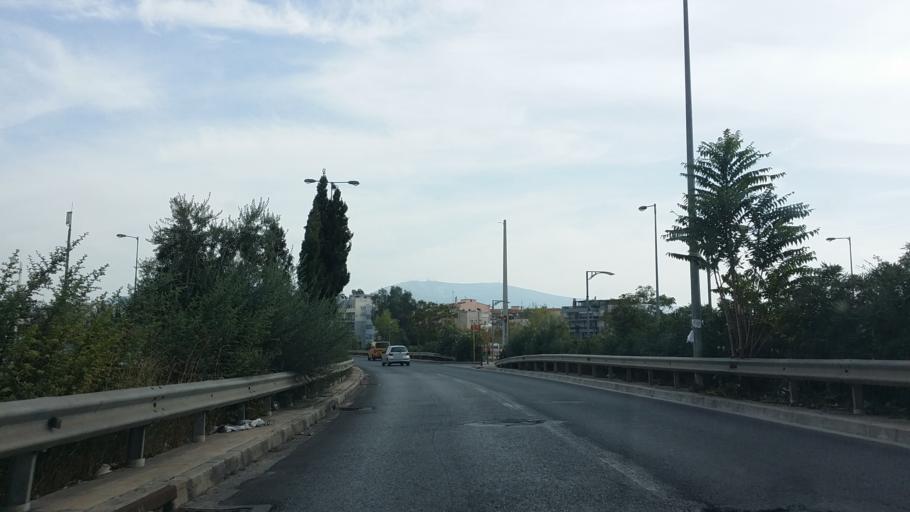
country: GR
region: Attica
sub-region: Nomarchia Athinas
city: Filothei
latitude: 38.0366
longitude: 23.7805
